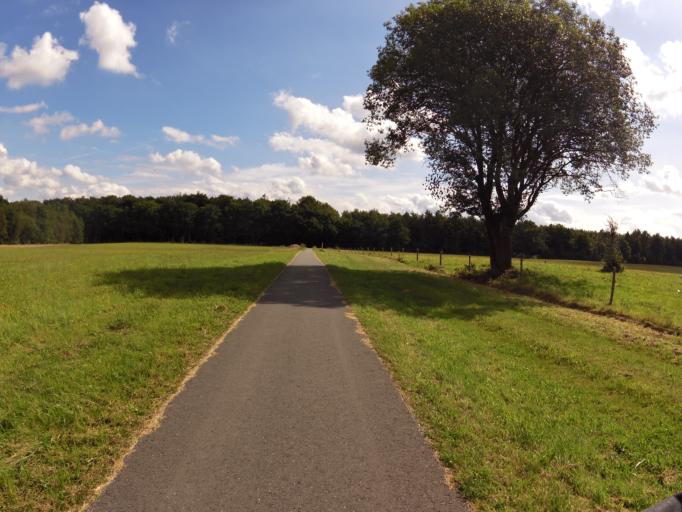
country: NL
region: Drenthe
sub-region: Gemeente Aa en Hunze
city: Anloo
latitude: 52.9888
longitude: 6.7146
